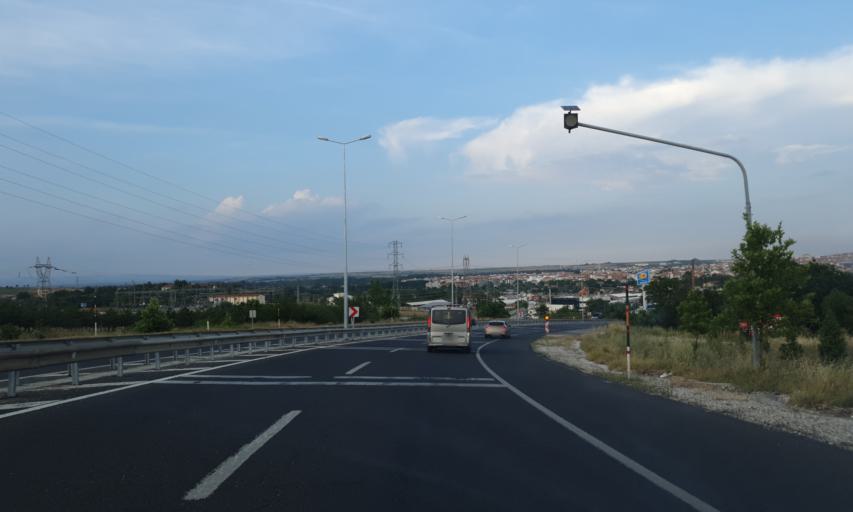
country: TR
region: Kirklareli
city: Luleburgaz
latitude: 41.4054
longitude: 27.3331
